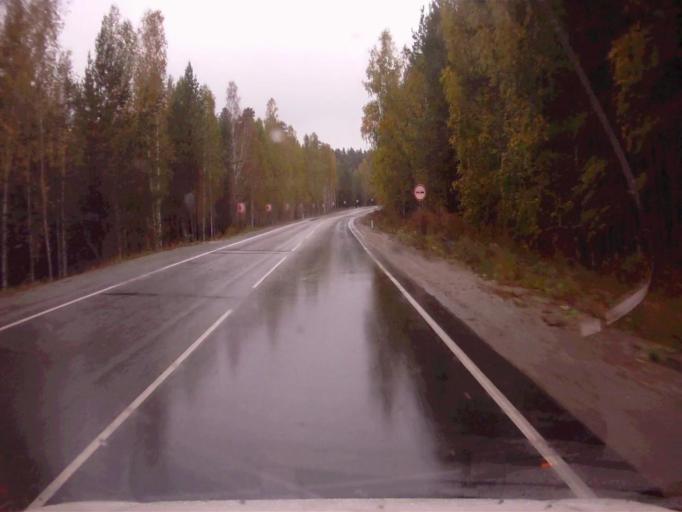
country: RU
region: Chelyabinsk
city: Kyshtym
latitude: 55.6548
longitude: 60.5751
